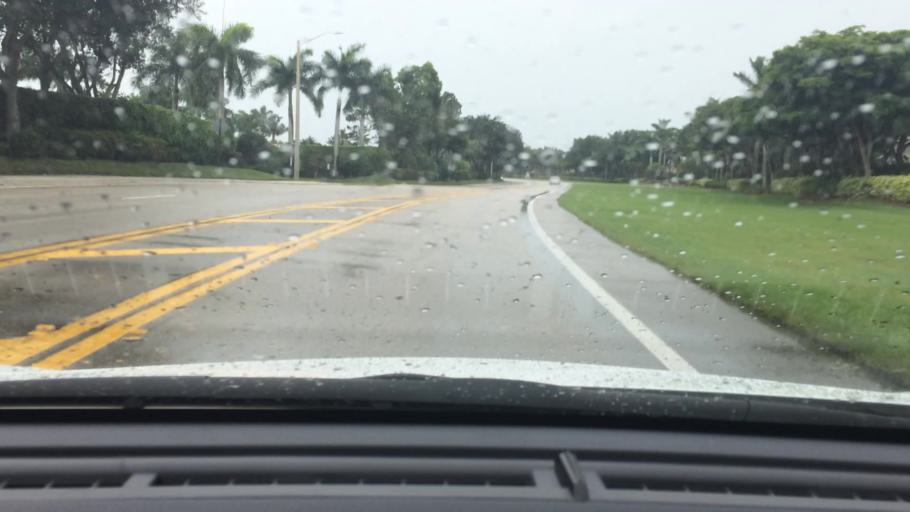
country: US
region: Florida
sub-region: Palm Beach County
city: Seminole Manor
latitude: 26.5465
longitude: -80.1615
